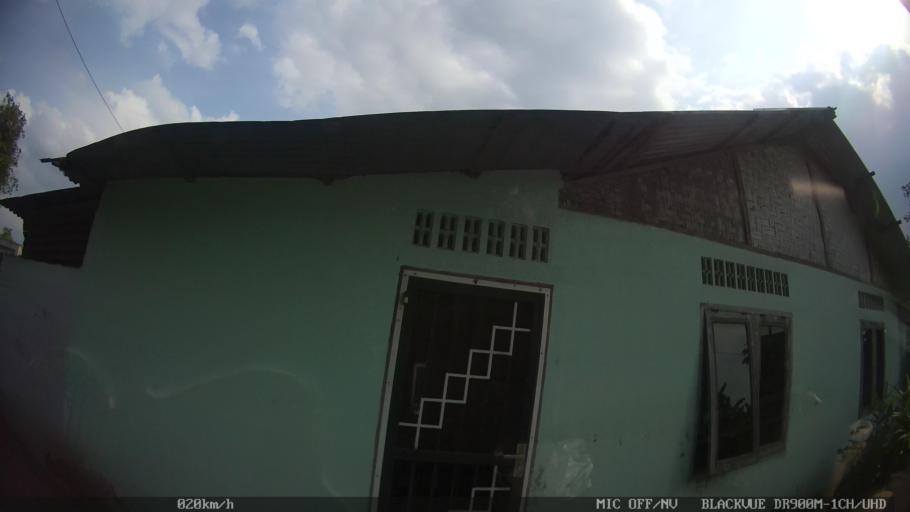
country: ID
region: North Sumatra
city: Binjai
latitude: 3.6038
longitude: 98.4928
